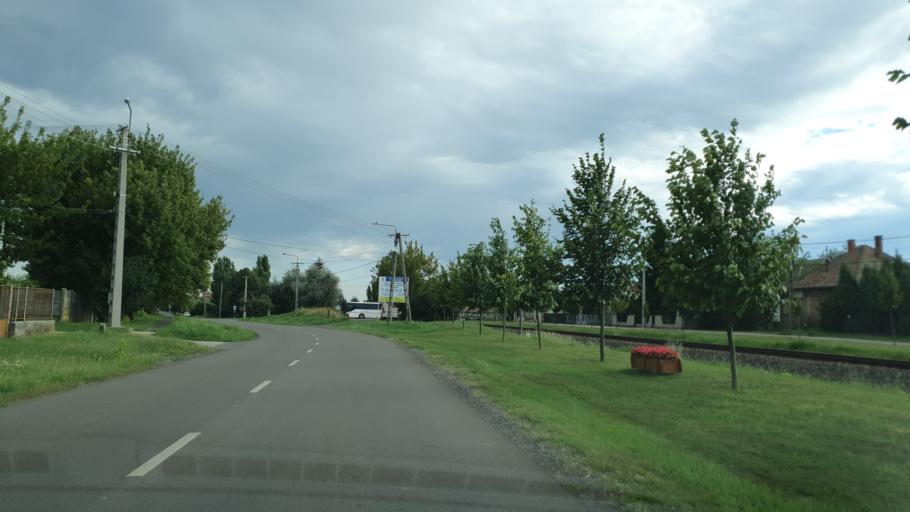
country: HU
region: Heves
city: Zagyvaszanto
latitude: 47.7702
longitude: 19.6695
